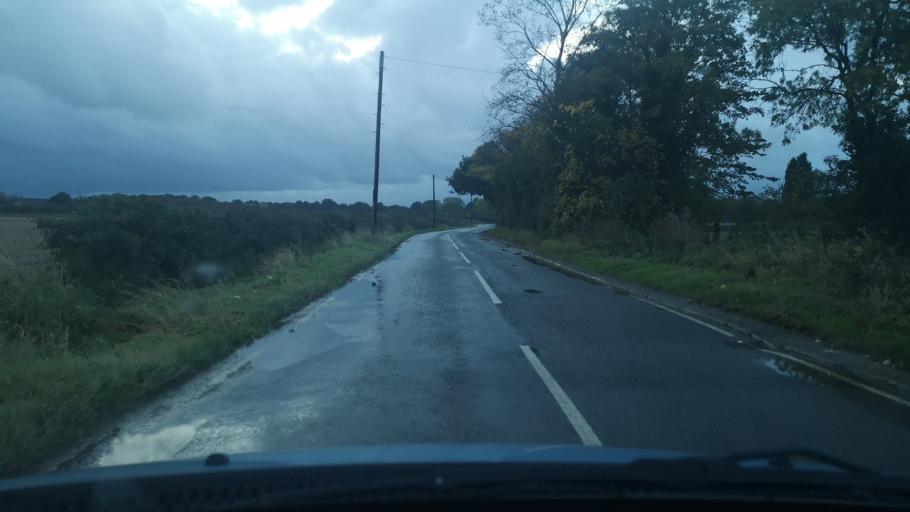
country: GB
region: England
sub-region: City and Borough of Wakefield
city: Low Ackworth
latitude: 53.6489
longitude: -1.3041
